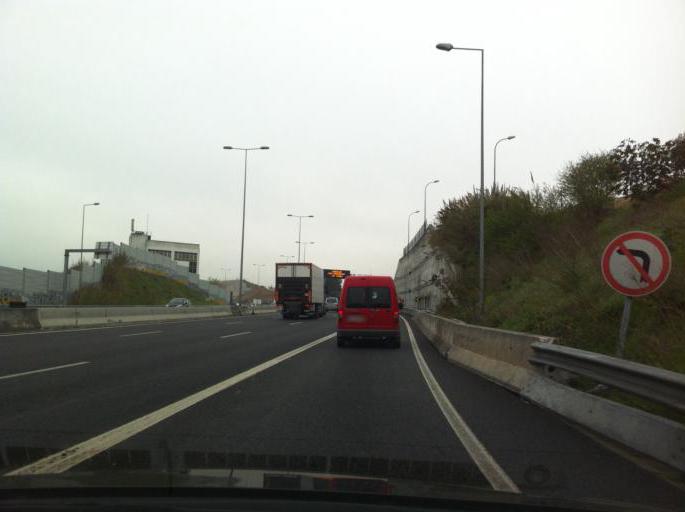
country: PT
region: Lisbon
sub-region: Odivelas
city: Pontinha
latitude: 38.7663
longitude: -9.2104
